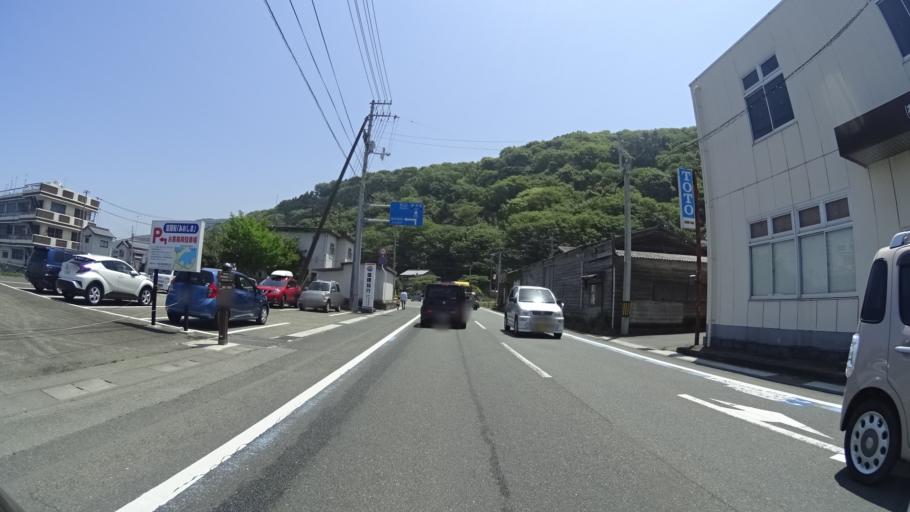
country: JP
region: Ehime
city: Ozu
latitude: 33.6150
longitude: 132.4839
